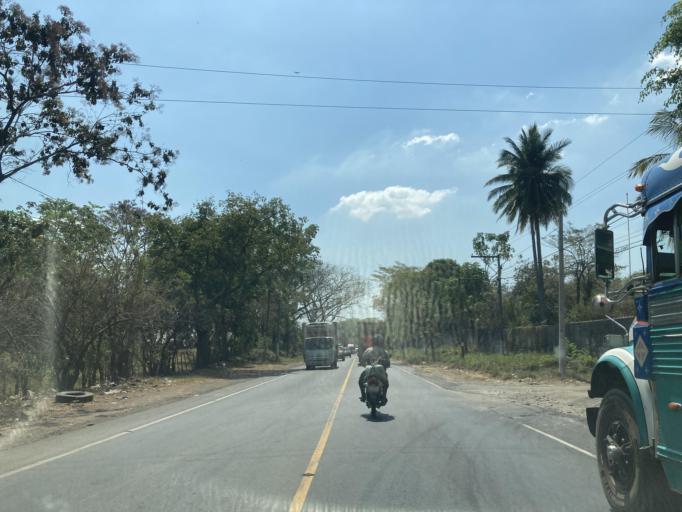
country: GT
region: Escuintla
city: Guanagazapa
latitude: 14.2163
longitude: -90.7249
